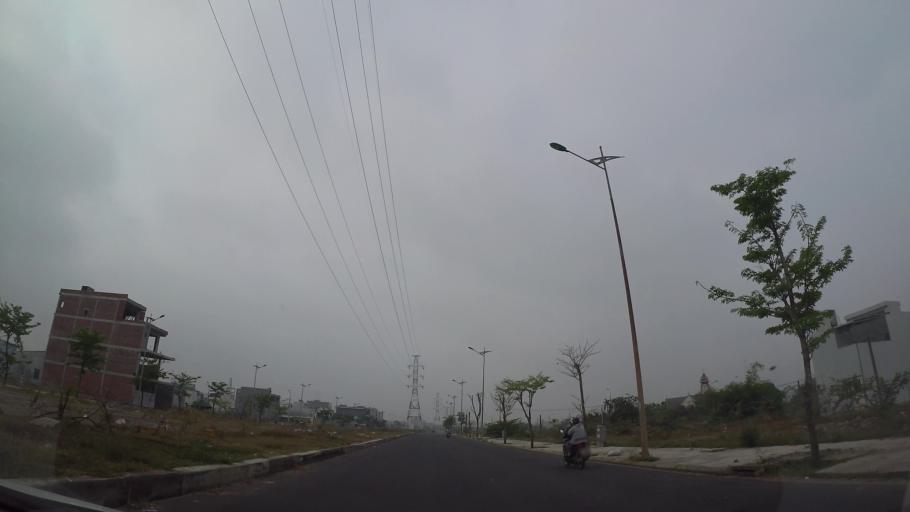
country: VN
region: Da Nang
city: Cam Le
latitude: 16.0154
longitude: 108.2275
